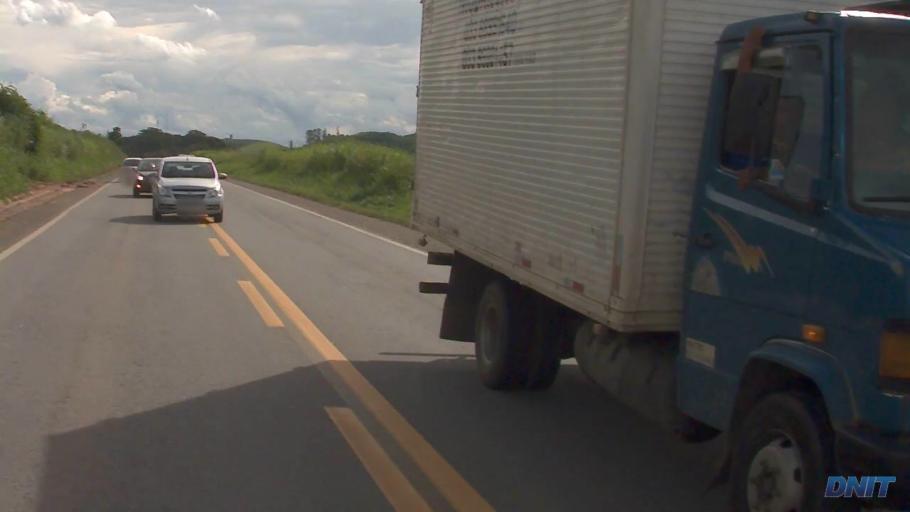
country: BR
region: Minas Gerais
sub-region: Belo Oriente
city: Belo Oriente
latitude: -19.2030
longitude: -42.2917
